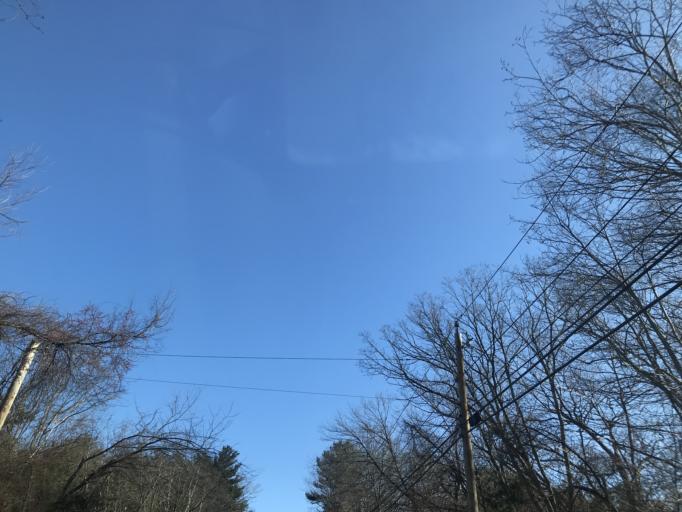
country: US
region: Massachusetts
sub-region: Essex County
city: Groveland
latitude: 42.7117
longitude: -71.0243
